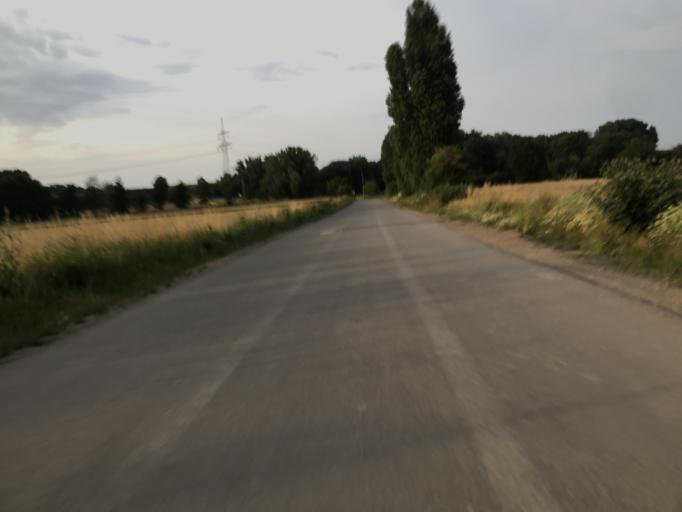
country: DE
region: Saxony-Anhalt
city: Quedlinburg
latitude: 51.8031
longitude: 11.1637
